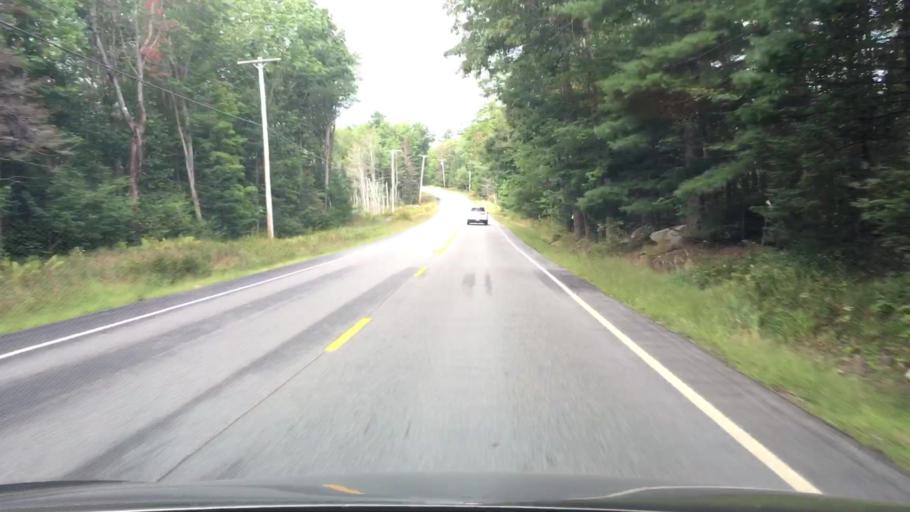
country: US
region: Maine
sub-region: Oxford County
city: Hartford
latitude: 44.3659
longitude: -70.3354
